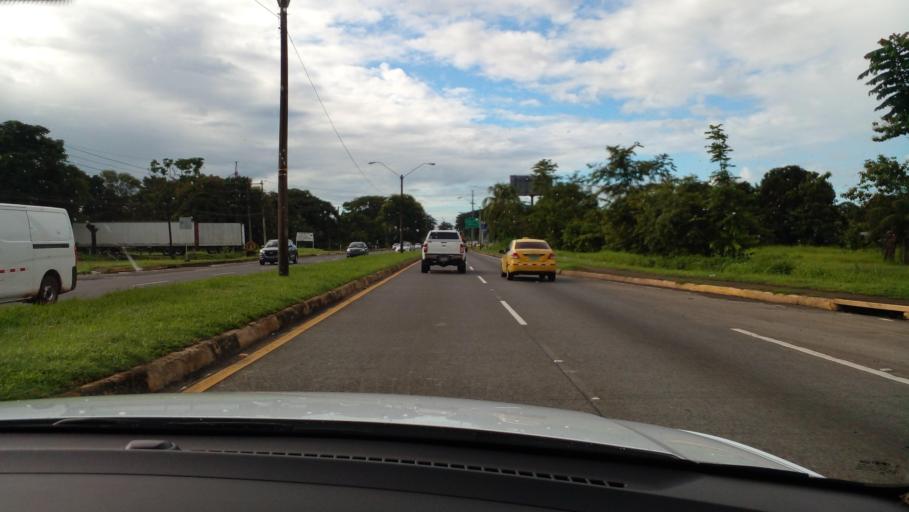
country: PA
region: Chiriqui
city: Las Lomas
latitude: 8.4382
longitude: -82.4141
